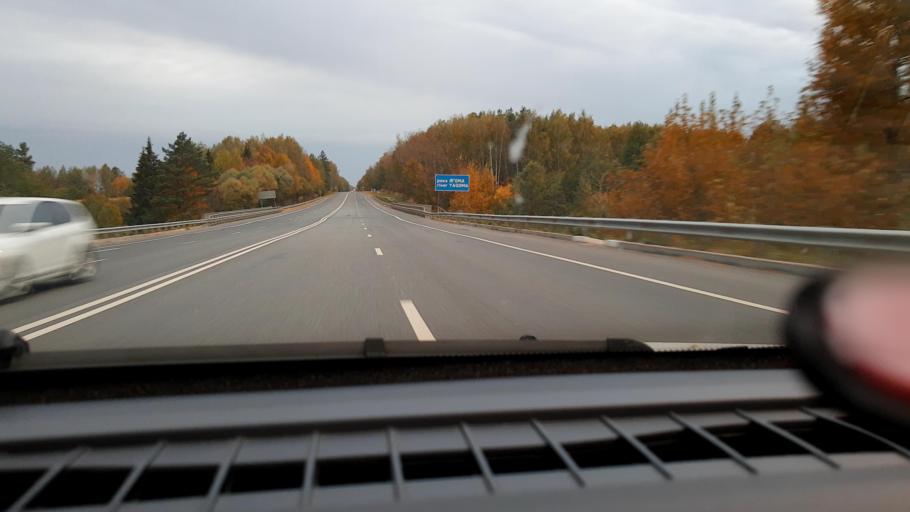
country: RU
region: Vladimir
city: Orgtrud
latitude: 56.2006
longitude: 40.8034
